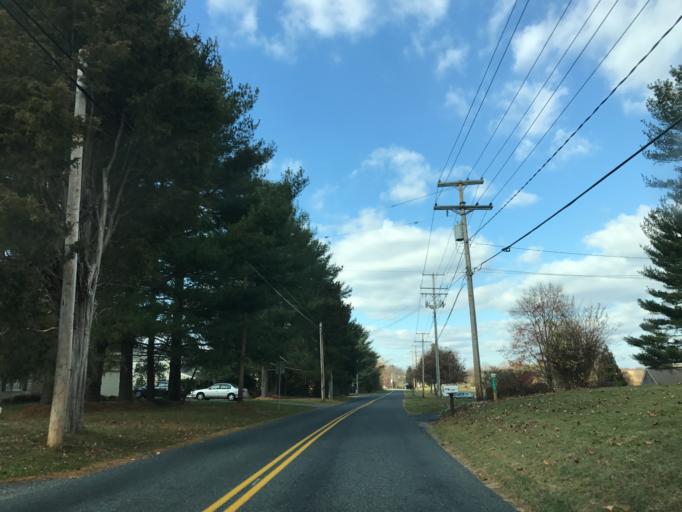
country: US
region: Maryland
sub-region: Harford County
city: Fallston
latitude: 39.5172
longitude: -76.4132
